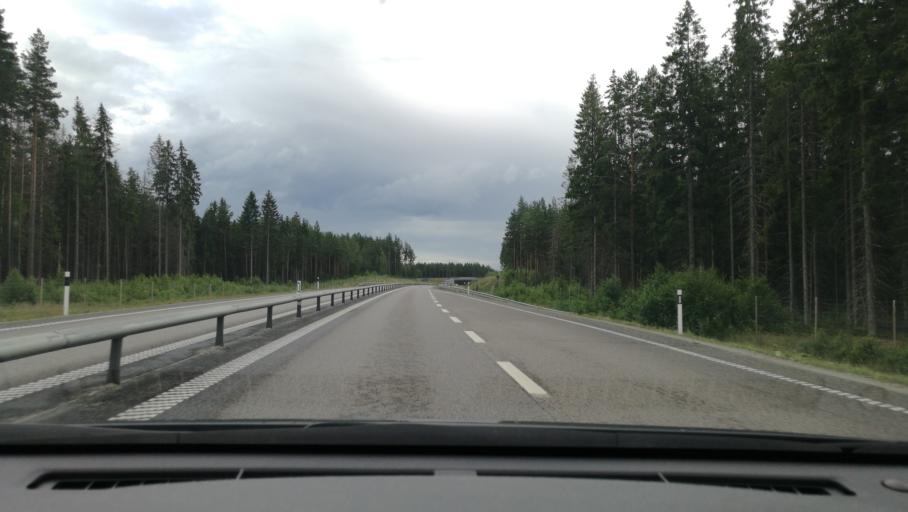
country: SE
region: Soedermanland
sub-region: Katrineholms Kommun
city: Katrineholm
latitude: 58.9904
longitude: 16.2629
